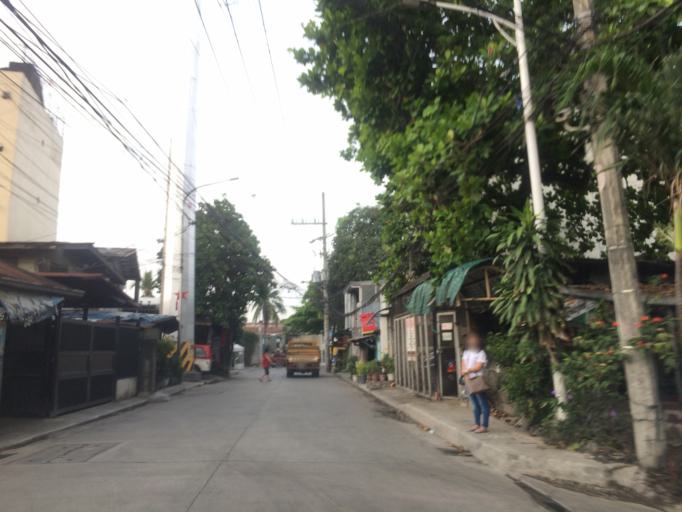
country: PH
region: Calabarzon
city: Del Monte
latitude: 14.6483
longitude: 121.0095
